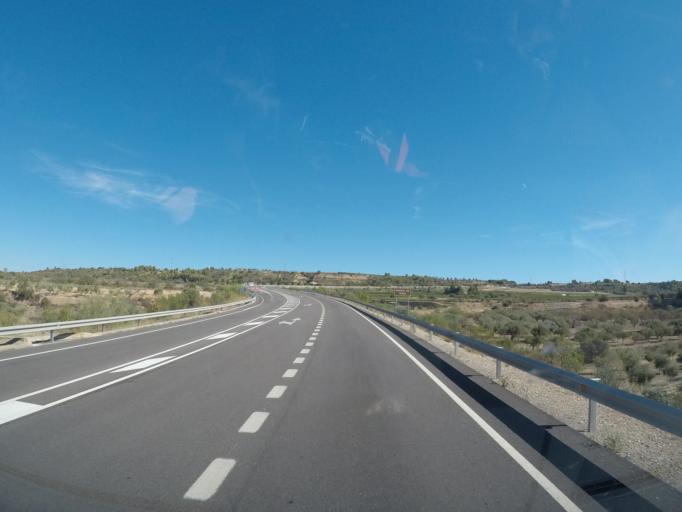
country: ES
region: Catalonia
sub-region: Provincia de Tarragona
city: Garcia
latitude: 41.0996
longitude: 0.6601
